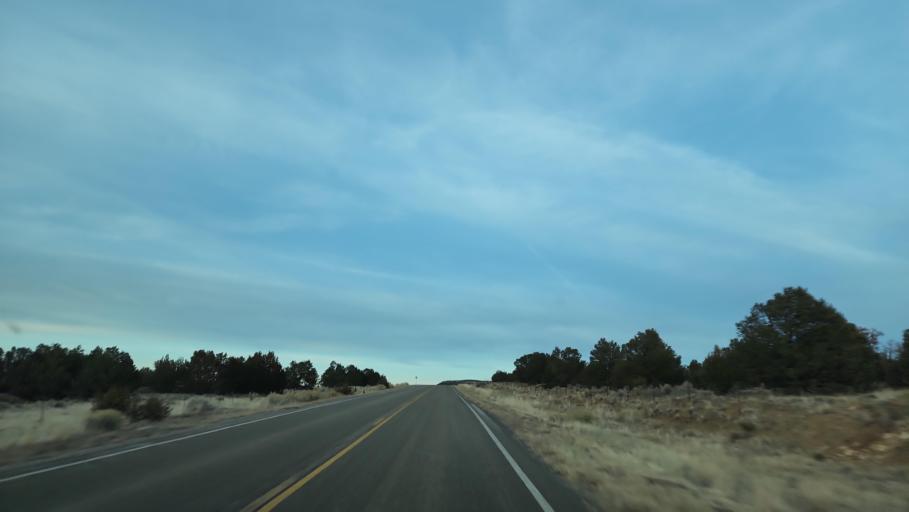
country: US
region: New Mexico
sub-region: Cibola County
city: Grants
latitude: 34.7209
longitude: -107.9798
